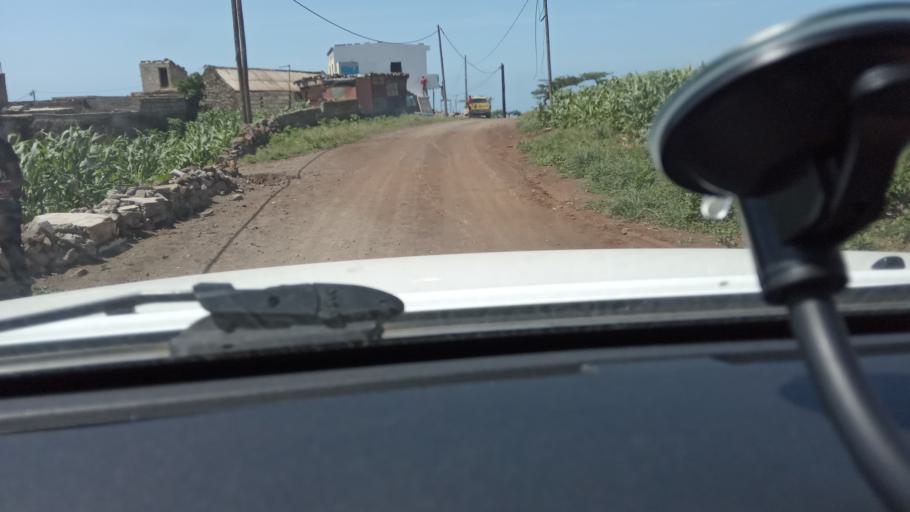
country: CV
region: Santa Catarina
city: Assomada
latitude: 15.0506
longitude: -23.7021
